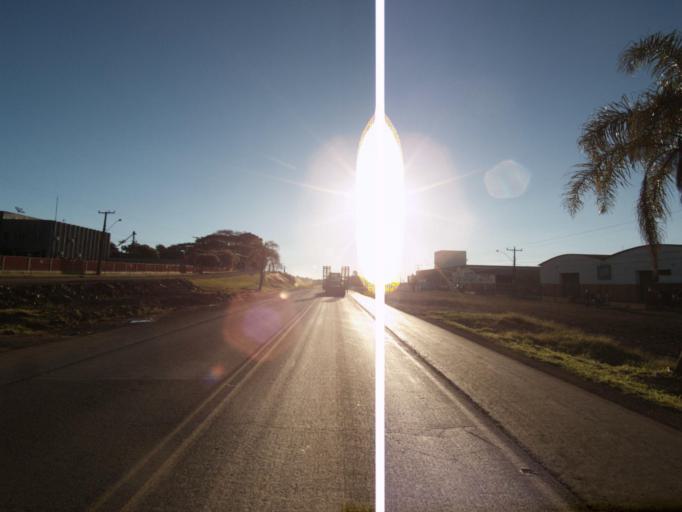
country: BR
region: Santa Catarina
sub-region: Chapeco
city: Chapeco
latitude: -26.8646
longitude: -52.9711
